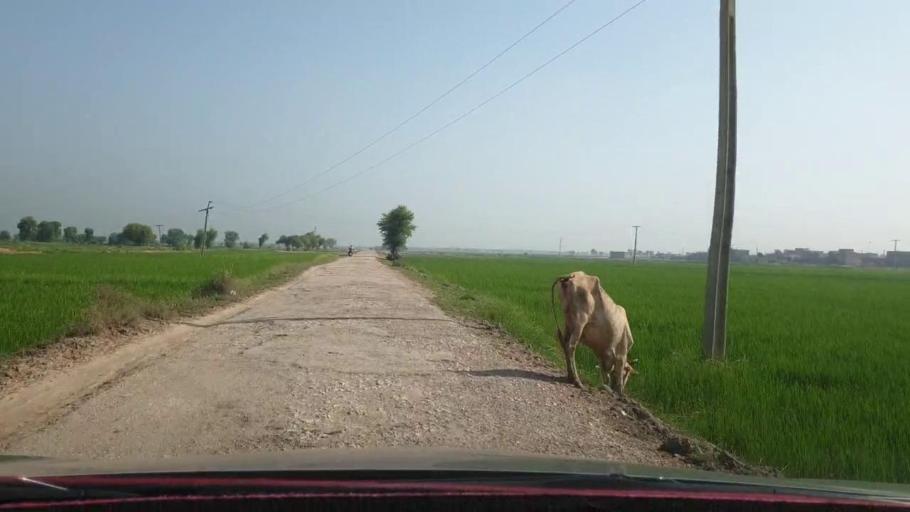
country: PK
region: Sindh
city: Nasirabad
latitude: 27.4924
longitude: 67.9283
